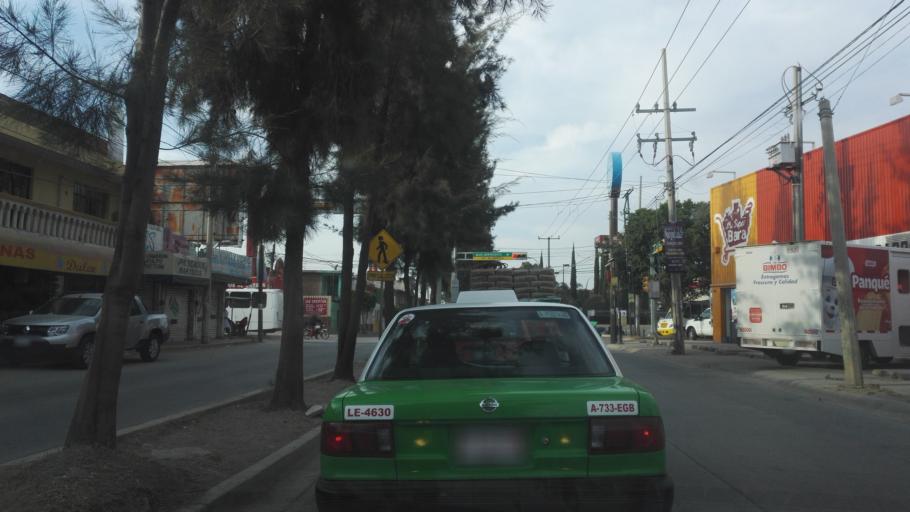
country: MX
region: Guanajuato
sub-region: Leon
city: Fraccionamiento Paraiso Real
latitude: 21.0977
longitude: -101.6036
